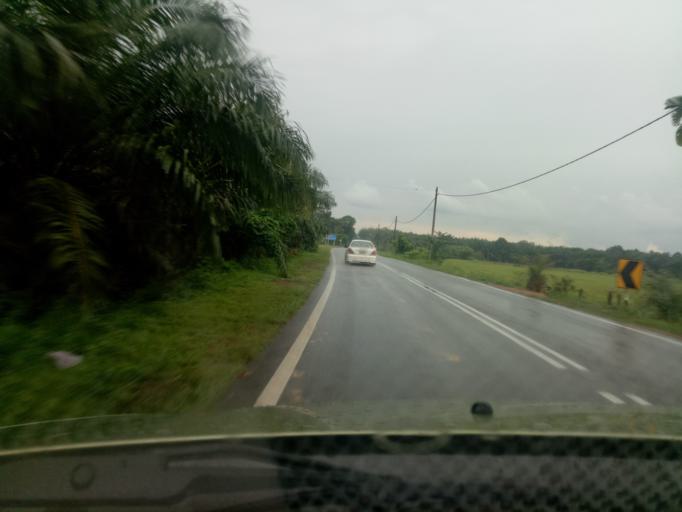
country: MY
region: Penang
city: Tasek Glugor
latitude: 5.5360
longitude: 100.5692
